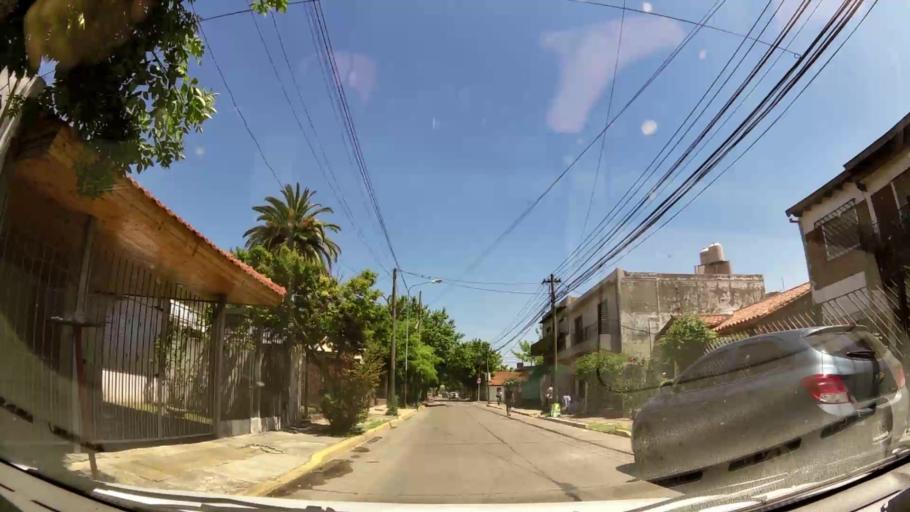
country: AR
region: Buenos Aires
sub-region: Partido de Merlo
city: Merlo
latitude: -34.6646
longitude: -58.7078
